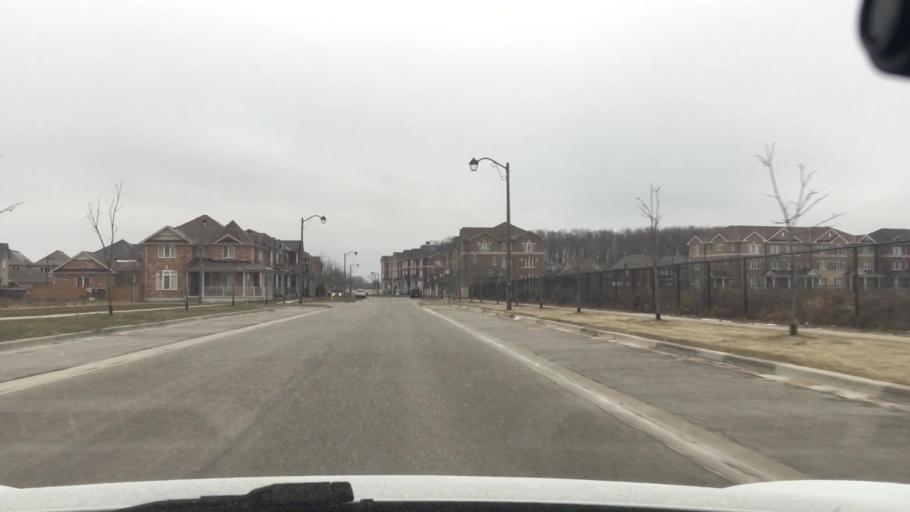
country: CA
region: Ontario
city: Markham
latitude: 43.8877
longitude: -79.2188
